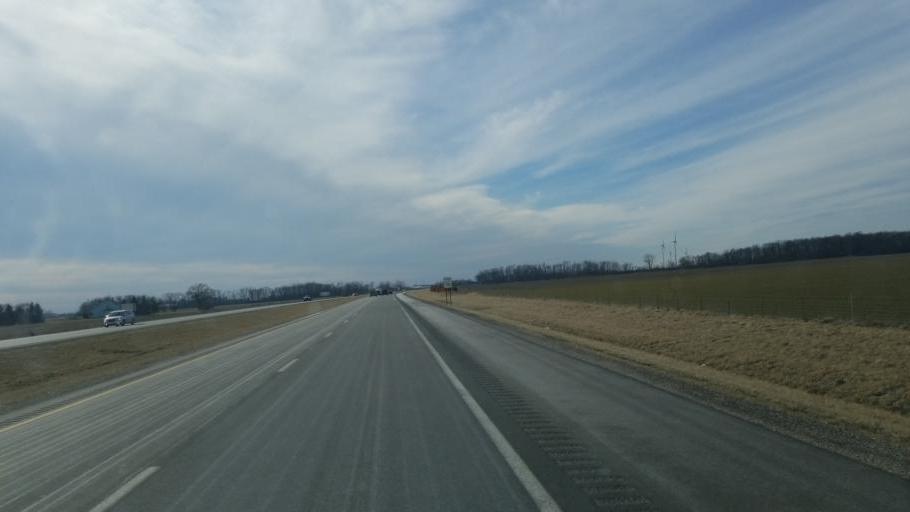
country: US
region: Ohio
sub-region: Van Wert County
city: Van Wert
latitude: 40.8961
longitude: -84.6324
